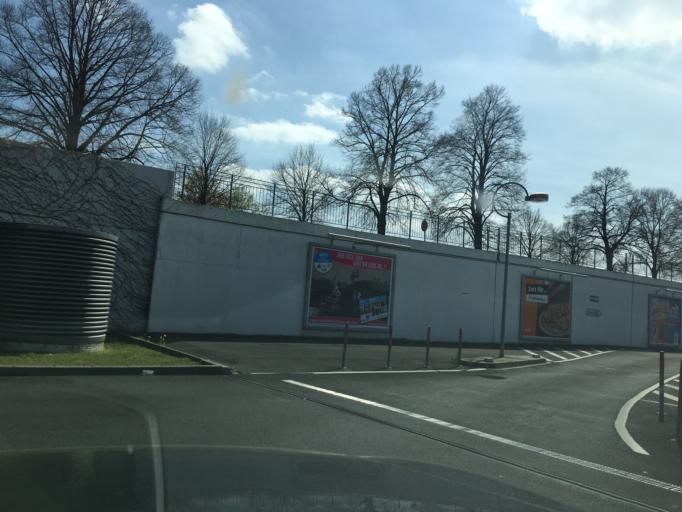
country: DE
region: North Rhine-Westphalia
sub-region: Regierungsbezirk Arnsberg
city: Holzwickede
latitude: 51.5137
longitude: 7.6111
